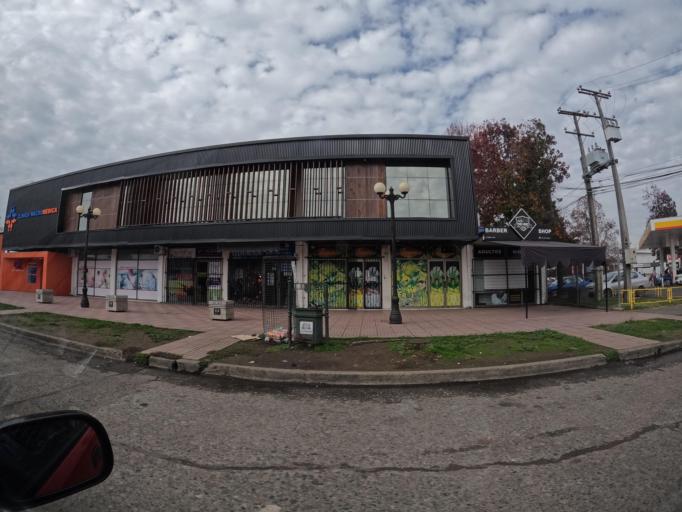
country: CL
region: Maule
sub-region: Provincia de Linares
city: Linares
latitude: -35.8466
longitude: -71.5911
